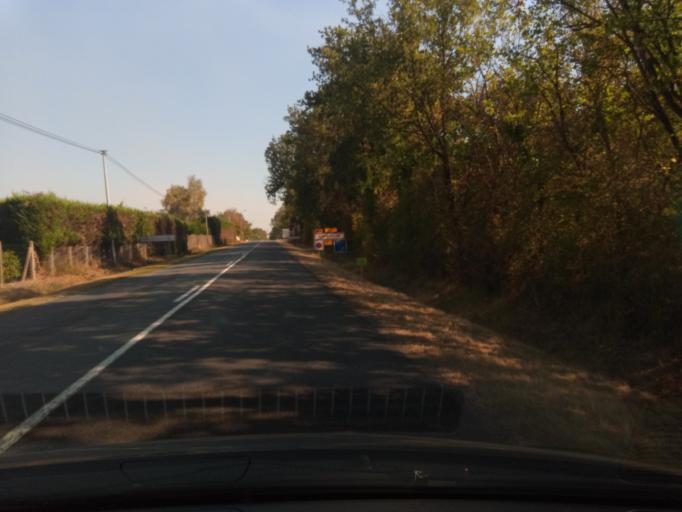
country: FR
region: Poitou-Charentes
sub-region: Departement de la Vienne
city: Montmorillon
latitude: 46.4288
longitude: 0.8541
